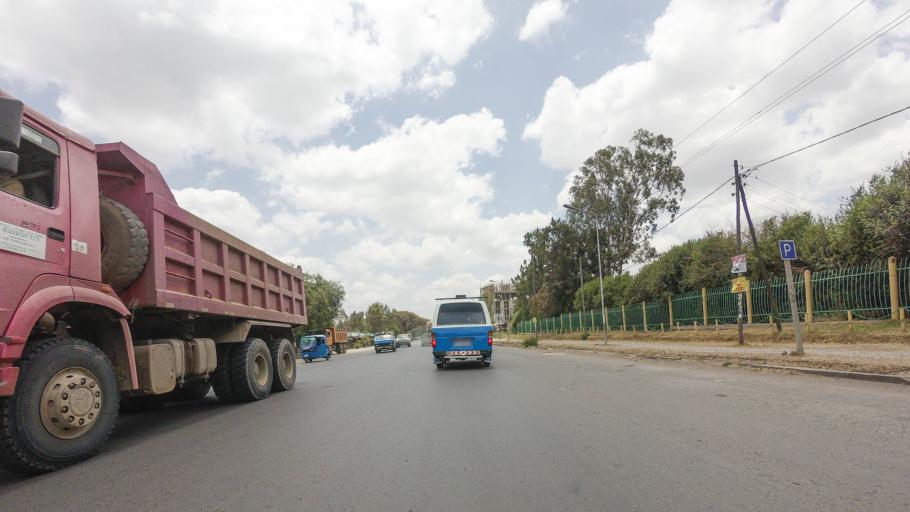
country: ET
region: Oromiya
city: Bishoftu
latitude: 8.7533
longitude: 38.9546
